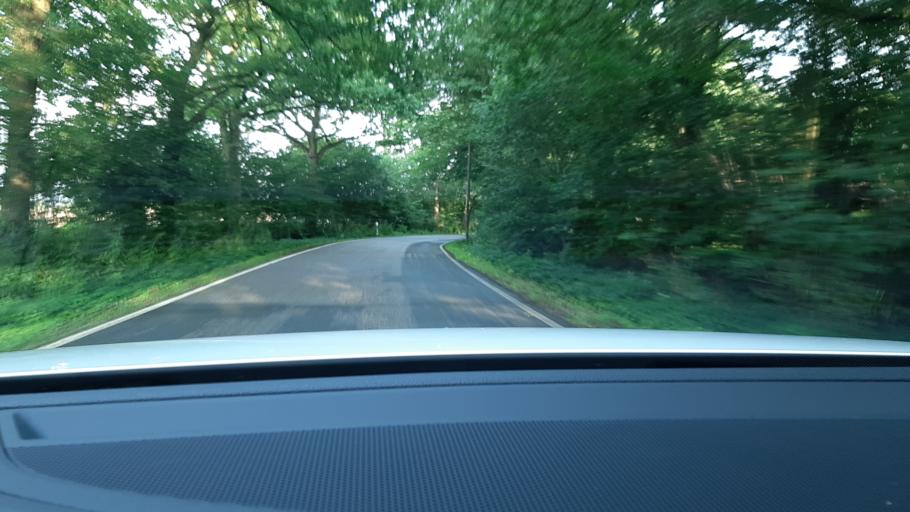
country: DE
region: Schleswig-Holstein
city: Stockelsdorf
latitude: 53.9287
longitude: 10.6066
